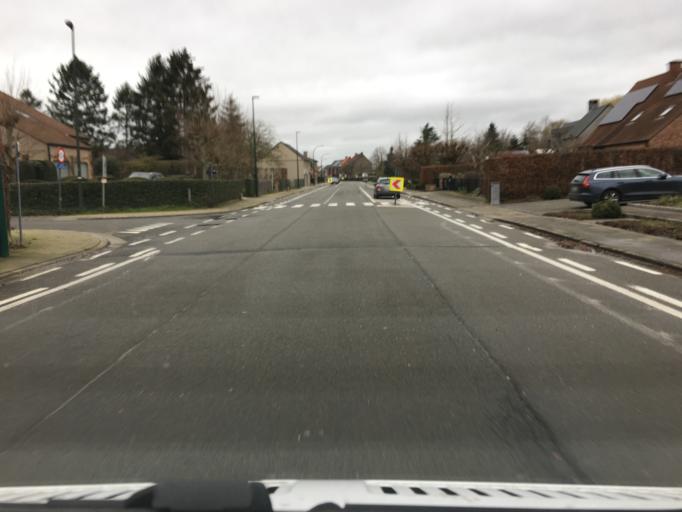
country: BE
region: Flanders
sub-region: Provincie Oost-Vlaanderen
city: Waarschoot
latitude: 51.1304
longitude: 3.6051
